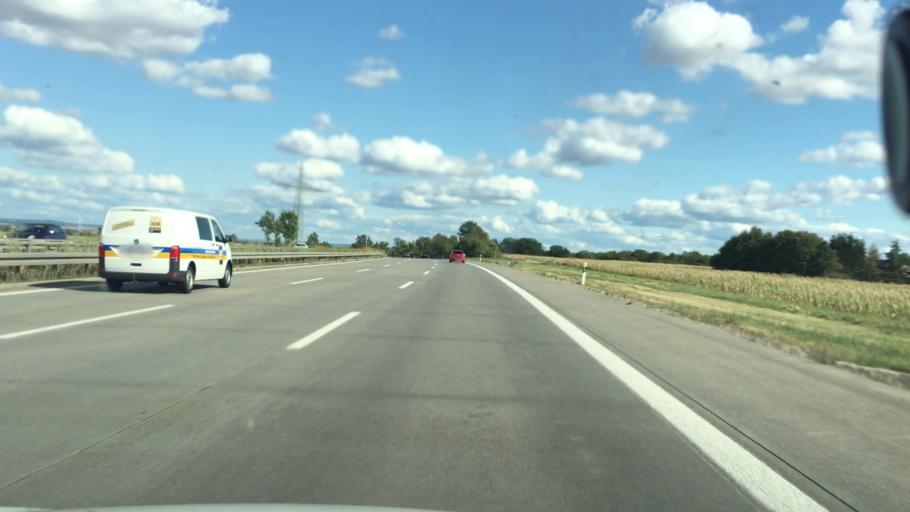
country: DE
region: Thuringia
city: Heyersdorf
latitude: 50.8377
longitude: 12.3632
